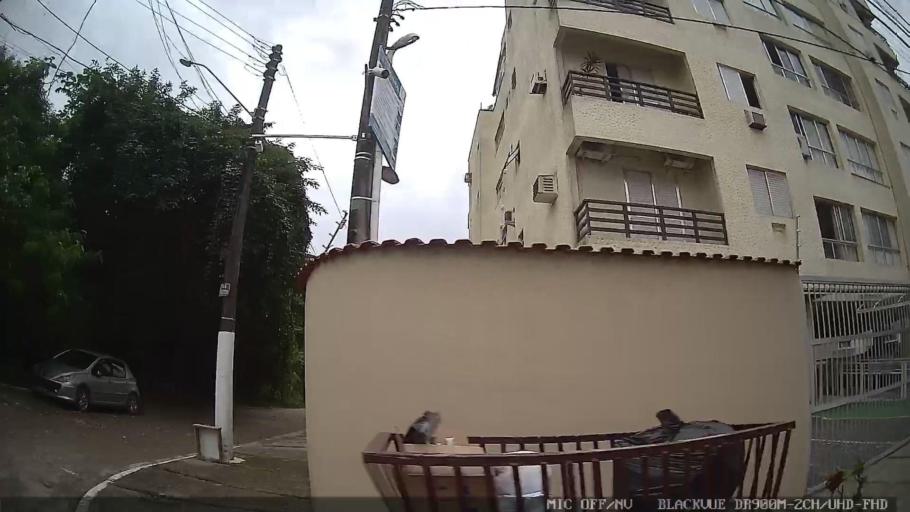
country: BR
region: Sao Paulo
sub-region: Guaruja
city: Guaruja
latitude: -24.0103
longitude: -46.2764
